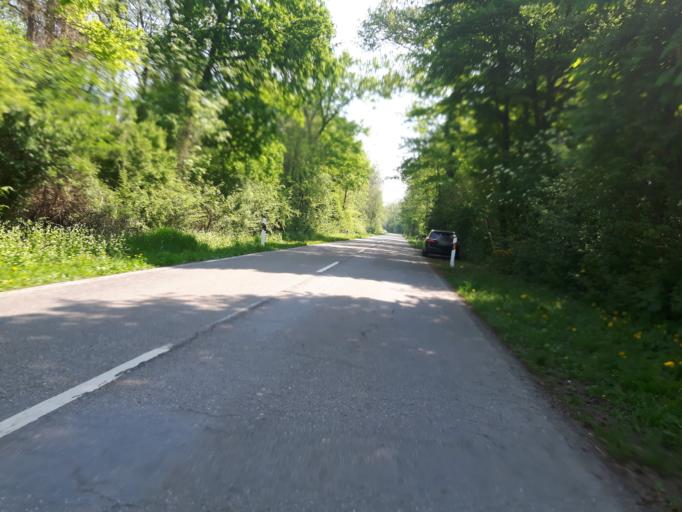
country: DE
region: Rheinland-Pfalz
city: Otterstadt
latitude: 49.3713
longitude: 8.4648
